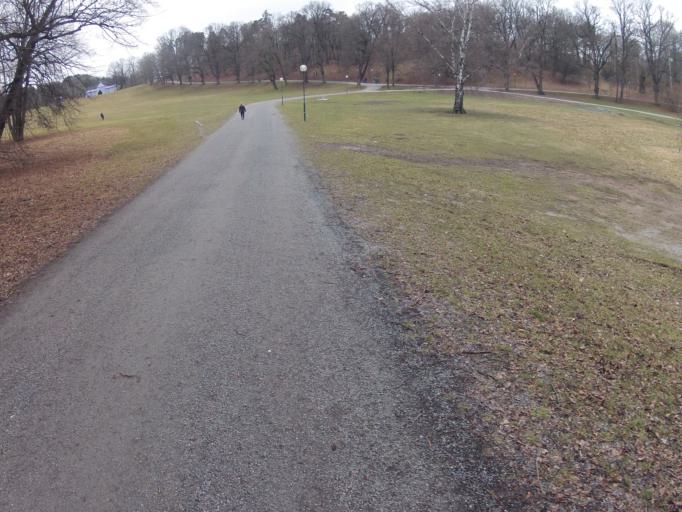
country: SE
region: Stockholm
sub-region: Norrtalje Kommun
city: Bergshamra
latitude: 59.3623
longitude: 18.0357
